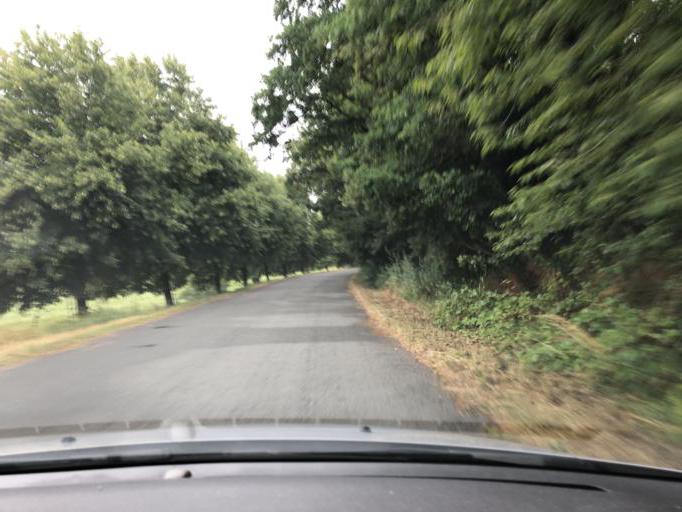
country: DE
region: Thuringia
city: Langenleuba-Niederhain
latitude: 50.9999
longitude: 12.6183
